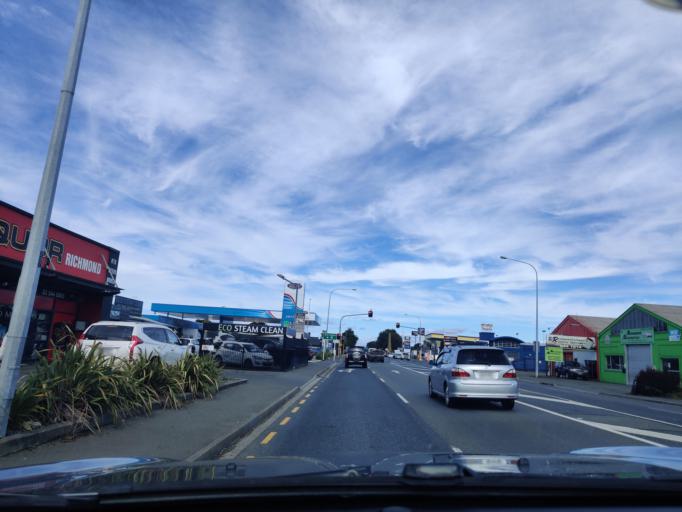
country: NZ
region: Tasman
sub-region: Tasman District
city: Richmond
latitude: -41.3369
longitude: 173.1814
